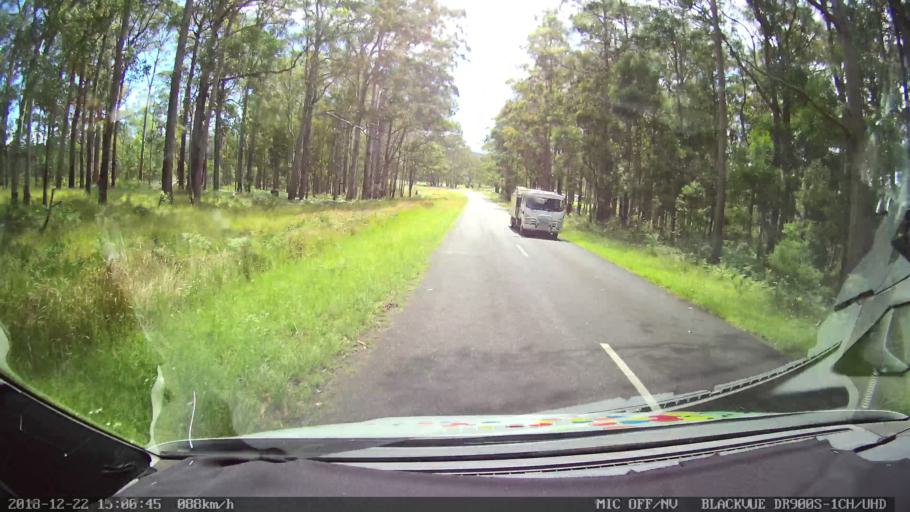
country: AU
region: New South Wales
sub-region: Bellingen
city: Dorrigo
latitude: -30.2496
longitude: 152.4660
